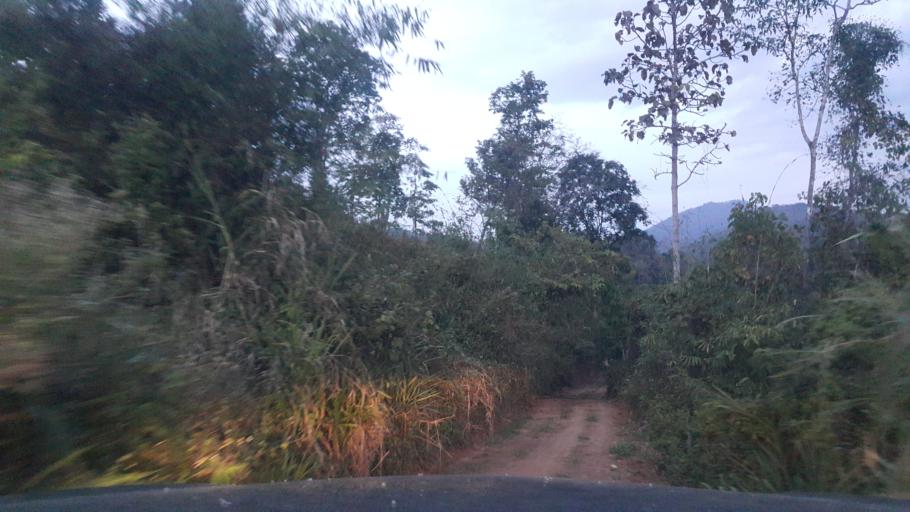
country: TH
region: Chiang Mai
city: Samoeng
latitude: 18.9479
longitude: 98.6726
